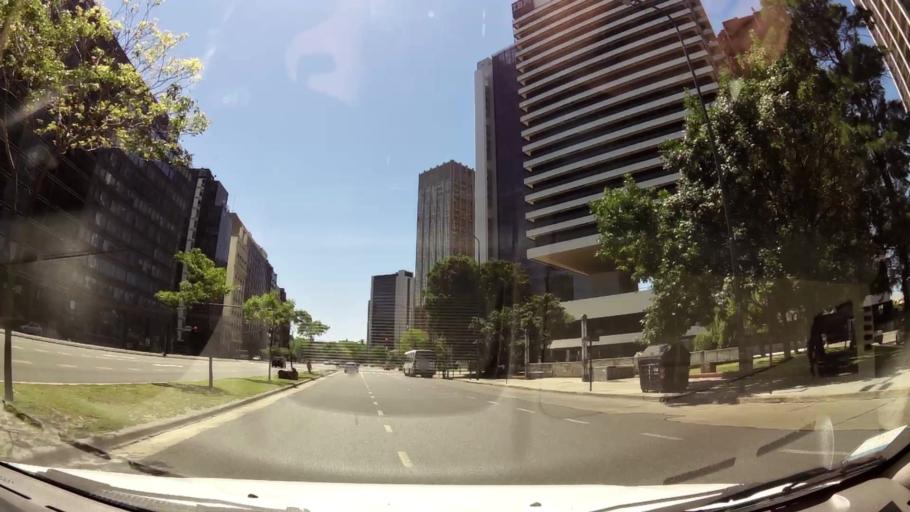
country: AR
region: Buenos Aires F.D.
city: Buenos Aires
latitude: -34.5968
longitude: -58.3719
